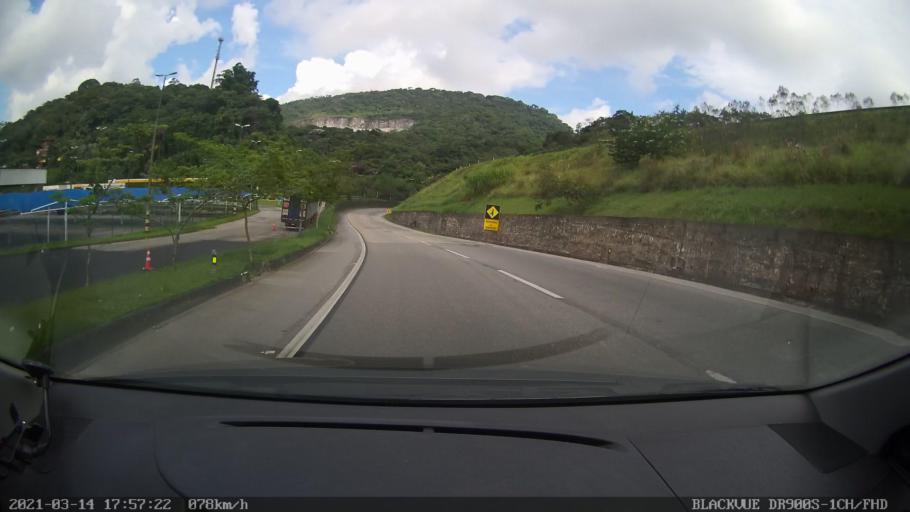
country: BR
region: Rio de Janeiro
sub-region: Petropolis
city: Petropolis
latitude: -22.5169
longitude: -43.2296
